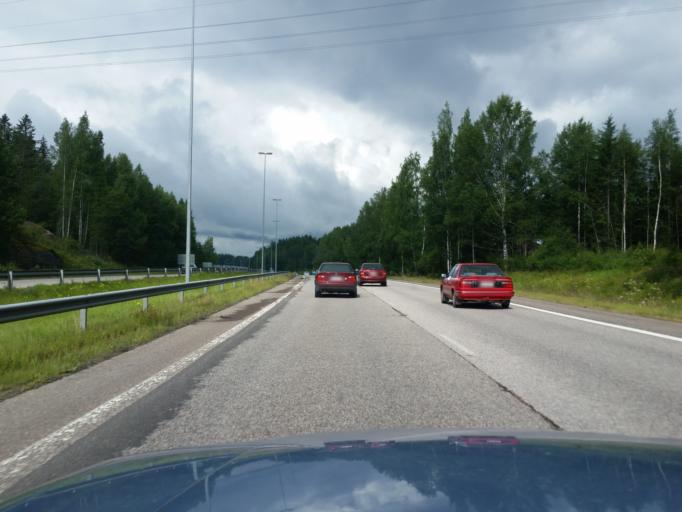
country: FI
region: Uusimaa
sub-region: Helsinki
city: Vihti
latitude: 60.2997
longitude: 24.2950
